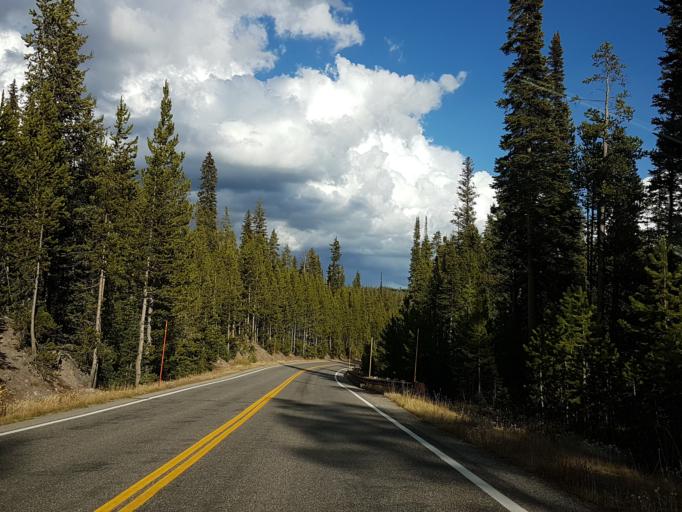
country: US
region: Montana
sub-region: Gallatin County
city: West Yellowstone
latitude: 44.4478
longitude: -110.7082
